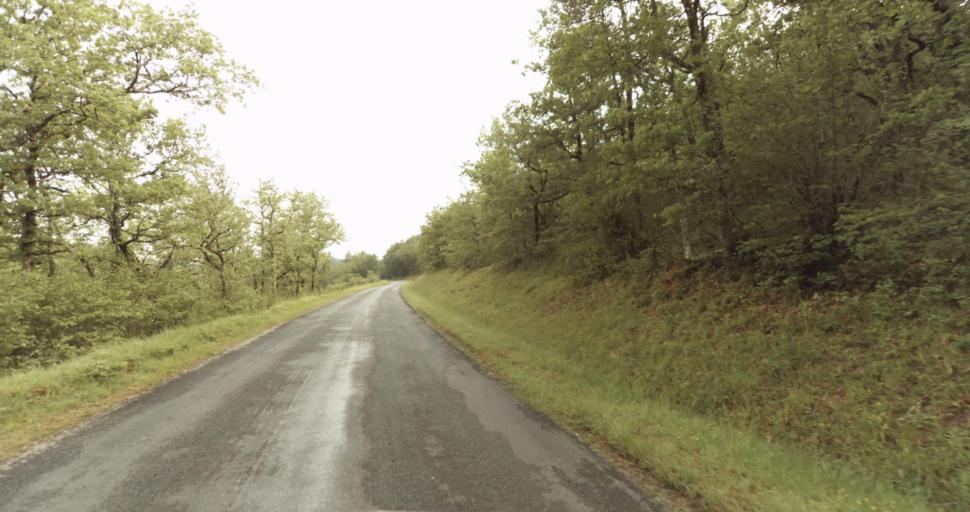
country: FR
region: Aquitaine
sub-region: Departement de la Dordogne
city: Lalinde
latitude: 44.8912
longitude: 0.7718
